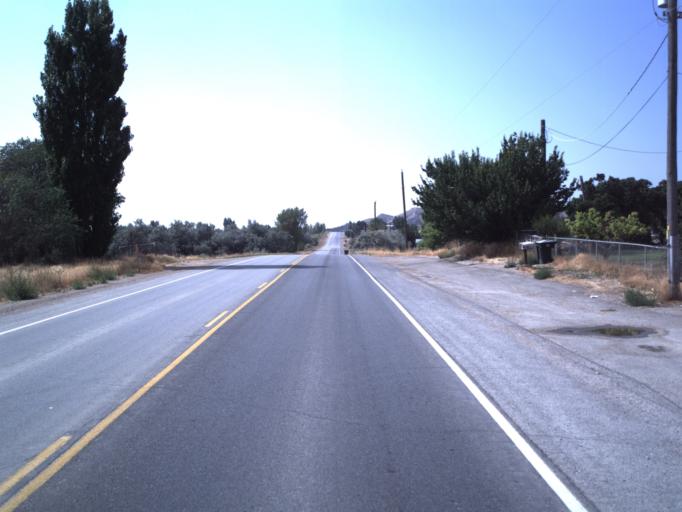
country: US
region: Utah
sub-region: Uintah County
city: Naples
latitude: 40.3775
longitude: -109.4985
